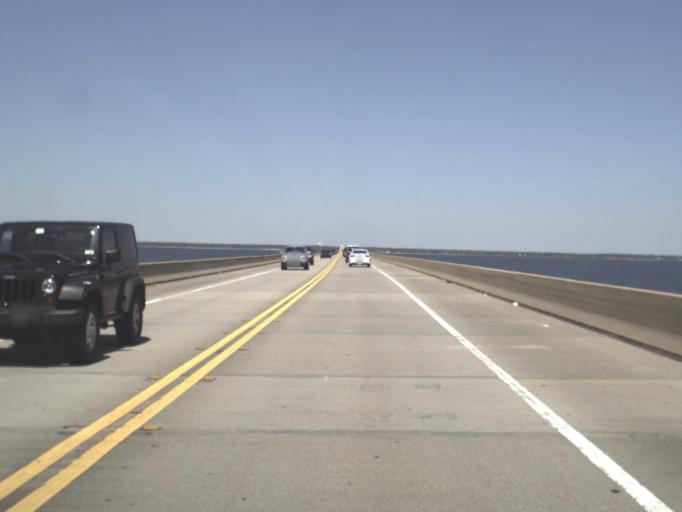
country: US
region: Florida
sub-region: Walton County
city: Miramar Beach
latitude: 30.4089
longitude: -86.4237
